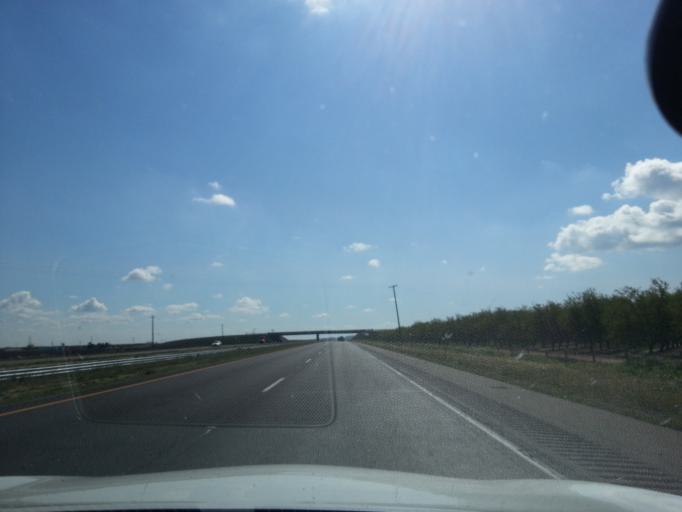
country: US
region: California
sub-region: Fresno County
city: Coalinga
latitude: 36.3734
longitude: -120.3387
